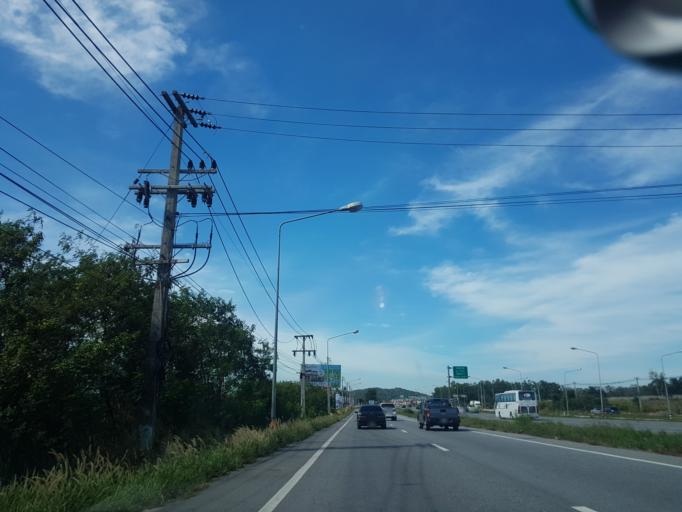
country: TH
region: Chon Buri
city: Phatthaya
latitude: 12.9114
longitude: 101.0262
